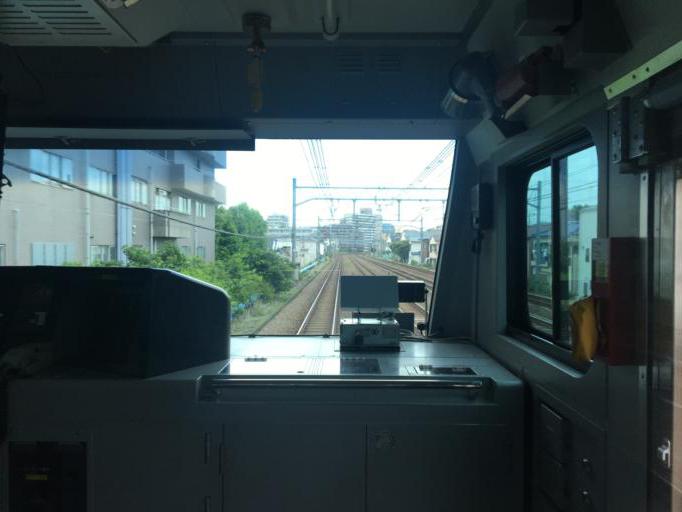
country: JP
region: Kanagawa
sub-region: Kawasaki-shi
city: Kawasaki
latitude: 35.6010
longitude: 139.7344
